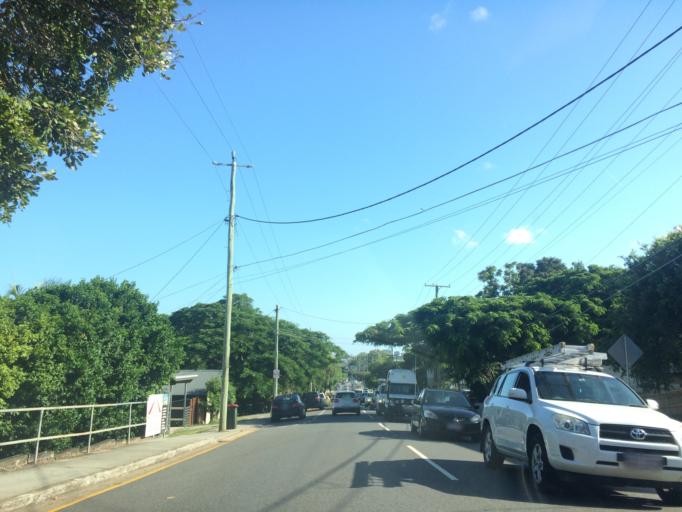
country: AU
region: Queensland
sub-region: Brisbane
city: Balmoral
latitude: -27.4686
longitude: 153.0592
